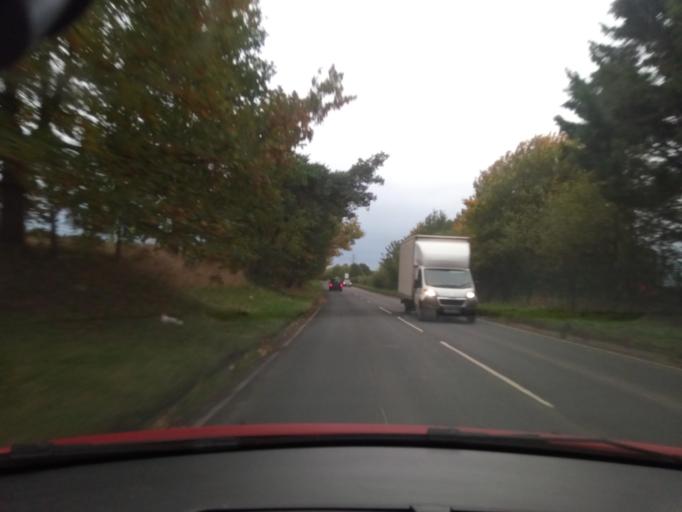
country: GB
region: England
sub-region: Essex
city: Great Yeldham
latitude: 51.9966
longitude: 0.5792
